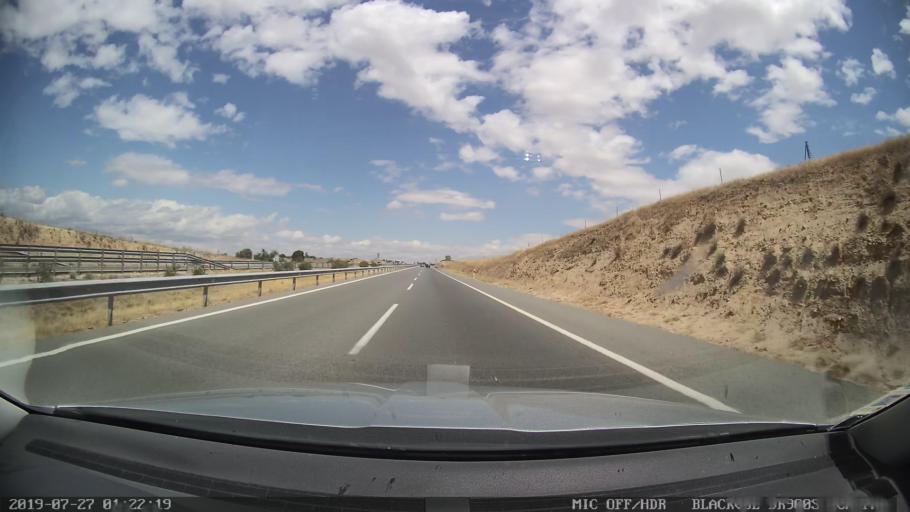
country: ES
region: Castille-La Mancha
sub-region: Province of Toledo
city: Santa Cruz del Retamar
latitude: 40.1202
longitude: -4.2590
